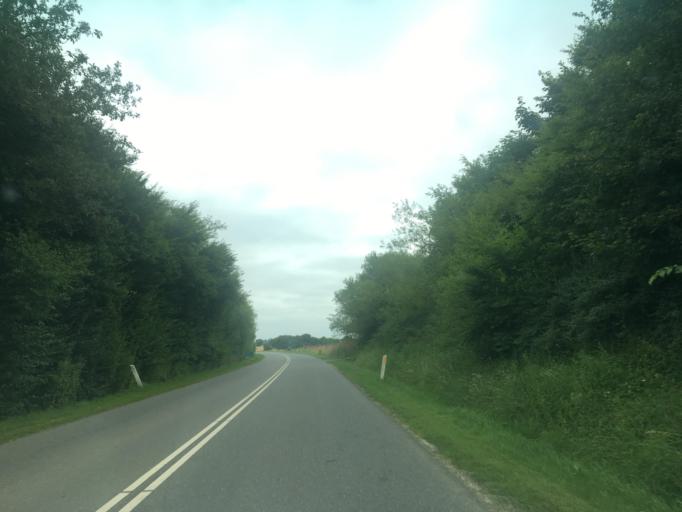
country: DK
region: North Denmark
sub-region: Thisted Kommune
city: Thisted
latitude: 56.8382
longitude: 8.5792
